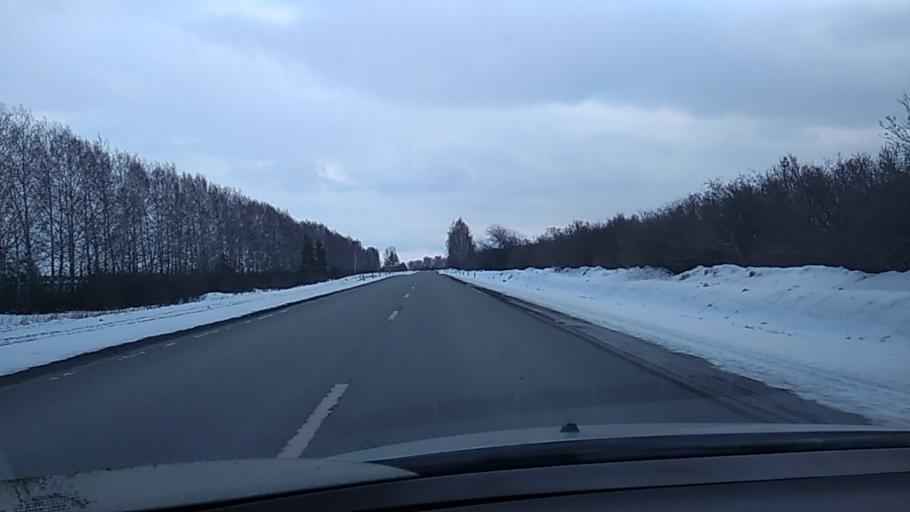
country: RU
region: Sverdlovsk
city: Sovkhoznyy
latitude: 56.5825
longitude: 61.3195
